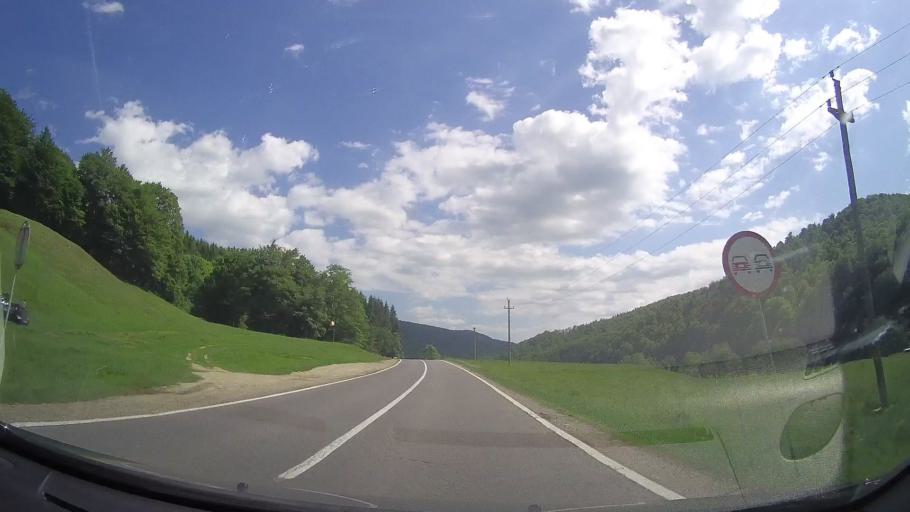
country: RO
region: Prahova
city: Maneciu
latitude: 45.4329
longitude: 25.9384
